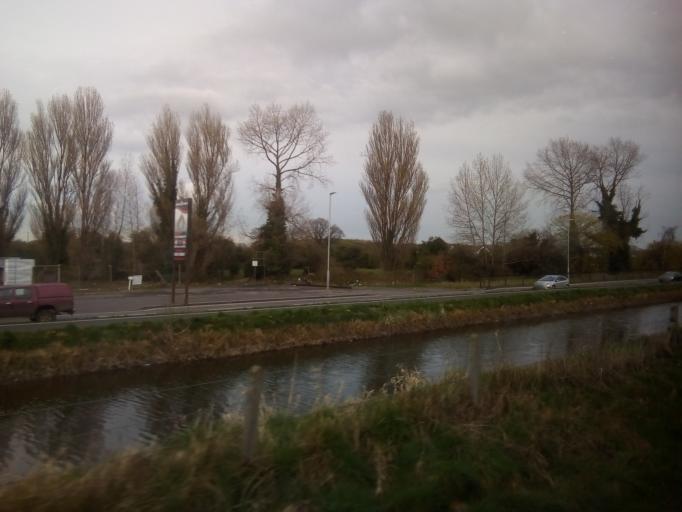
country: IE
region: Leinster
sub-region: Kildare
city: Kilcock
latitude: 53.3973
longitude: -6.6630
